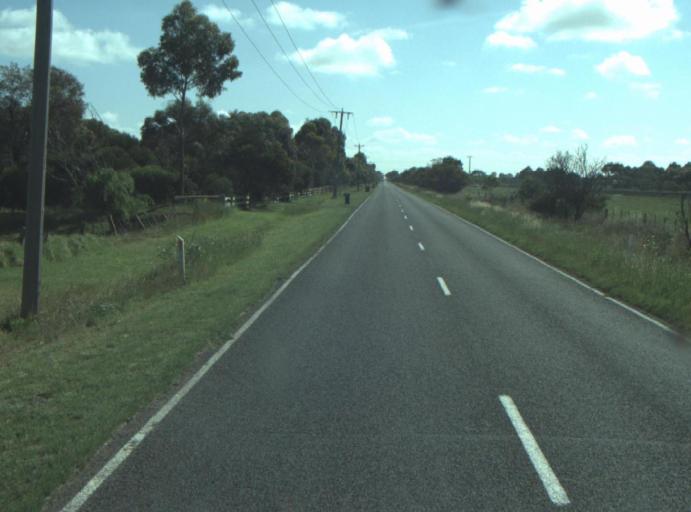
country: AU
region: Victoria
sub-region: Greater Geelong
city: Lara
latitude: -38.0147
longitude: 144.4224
